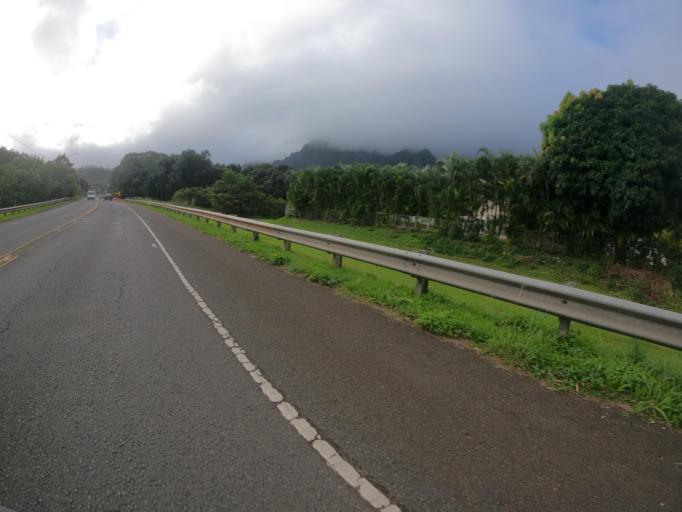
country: US
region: Hawaii
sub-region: Honolulu County
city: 'Ahuimanu
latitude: 21.4415
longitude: -157.8324
